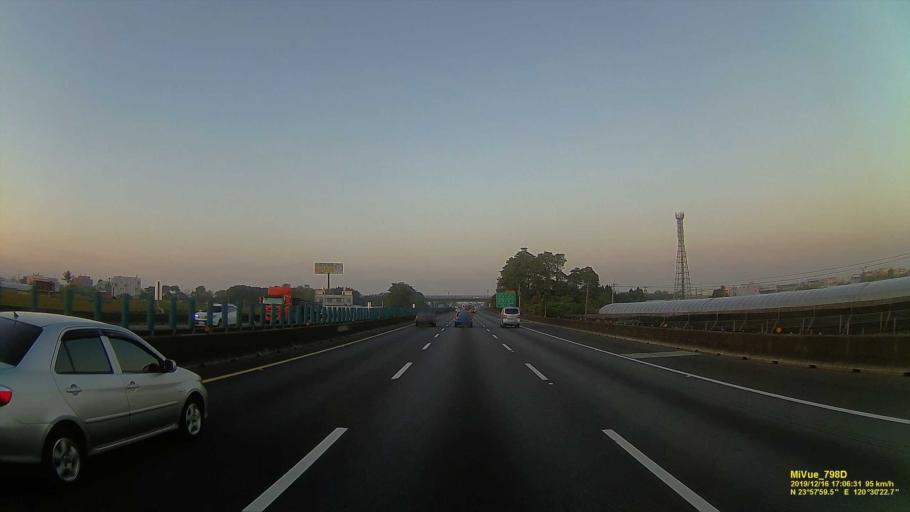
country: TW
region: Taiwan
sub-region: Changhua
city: Chang-hua
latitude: 23.9671
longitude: 120.5063
